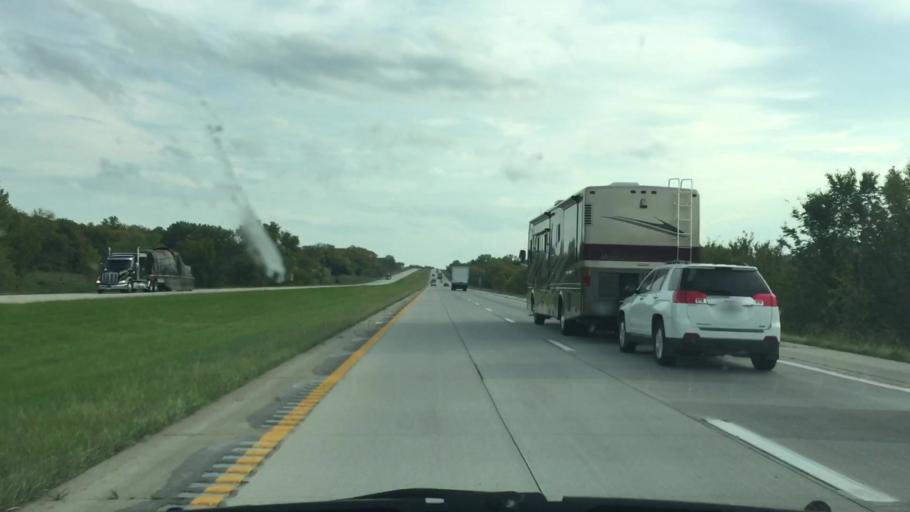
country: US
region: Missouri
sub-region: Daviess County
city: Gallatin
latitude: 39.9879
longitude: -94.0952
